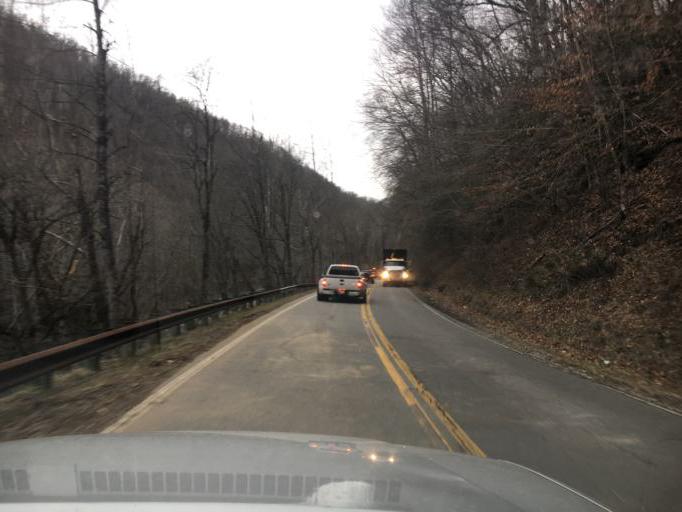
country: US
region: North Carolina
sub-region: Graham County
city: Robbinsville
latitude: 35.3133
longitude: -83.6398
